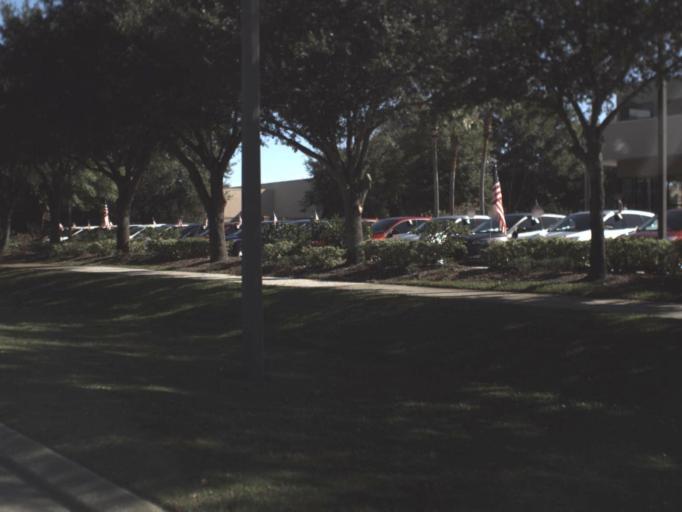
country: US
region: Florida
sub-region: Flagler County
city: Palm Coast
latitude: 29.5523
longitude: -81.2316
